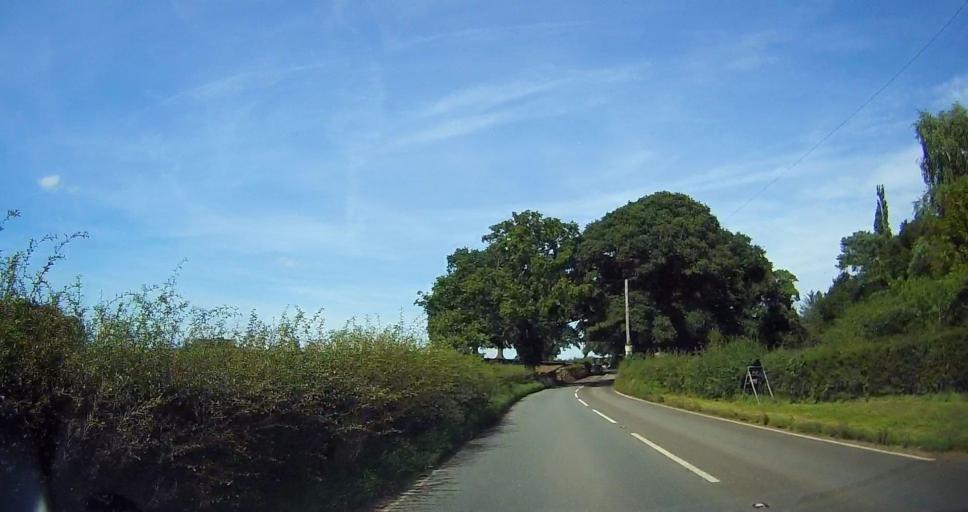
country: GB
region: England
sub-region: Shropshire
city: Market Drayton
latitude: 52.9639
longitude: -2.5157
